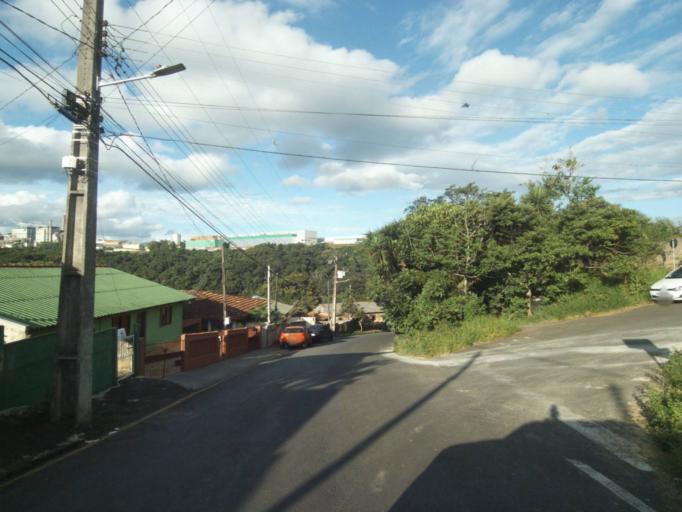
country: BR
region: Parana
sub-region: Telemaco Borba
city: Telemaco Borba
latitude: -24.3231
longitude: -50.6131
